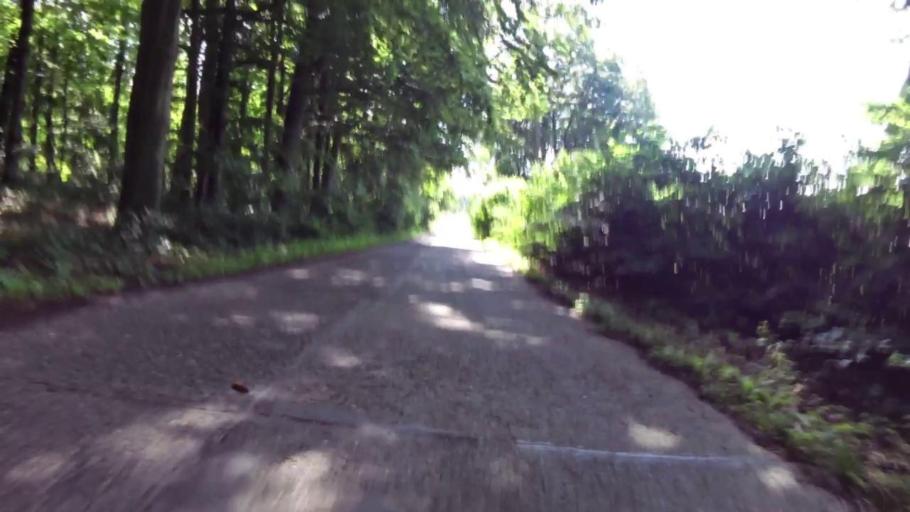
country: PL
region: West Pomeranian Voivodeship
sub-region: Powiat stargardzki
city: Dobrzany
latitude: 53.3905
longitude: 15.4867
